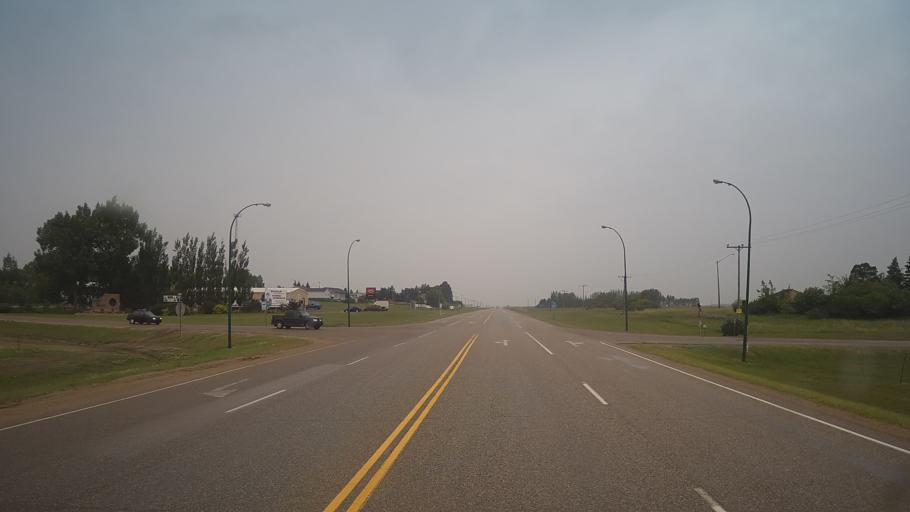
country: CA
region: Saskatchewan
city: Biggar
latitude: 52.0623
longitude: -107.9792
